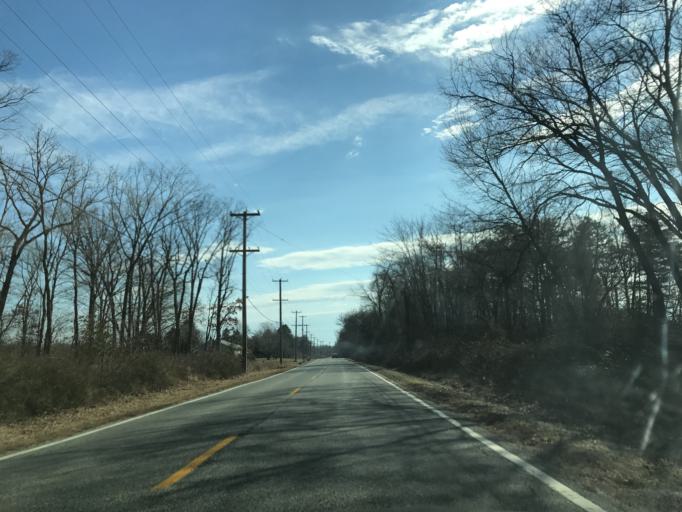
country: US
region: Maryland
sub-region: Cecil County
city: Charlestown
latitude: 39.5804
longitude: -76.0035
